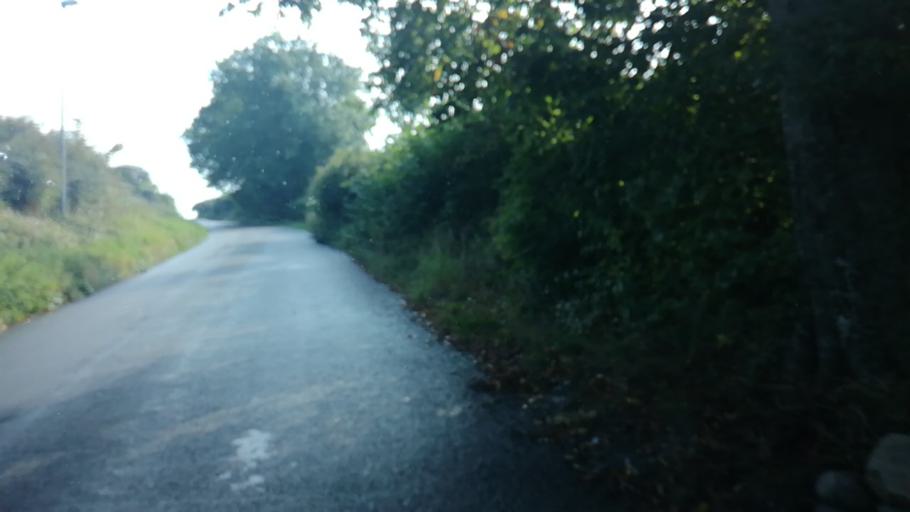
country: DK
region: South Denmark
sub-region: Fredericia Kommune
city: Fredericia
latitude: 55.6199
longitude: 9.7894
